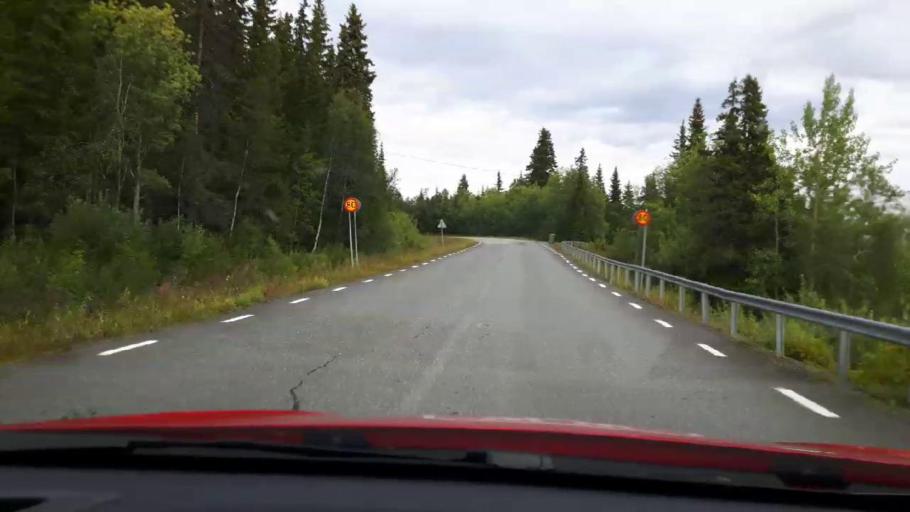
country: SE
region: Jaemtland
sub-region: Are Kommun
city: Are
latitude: 63.7028
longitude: 12.9492
